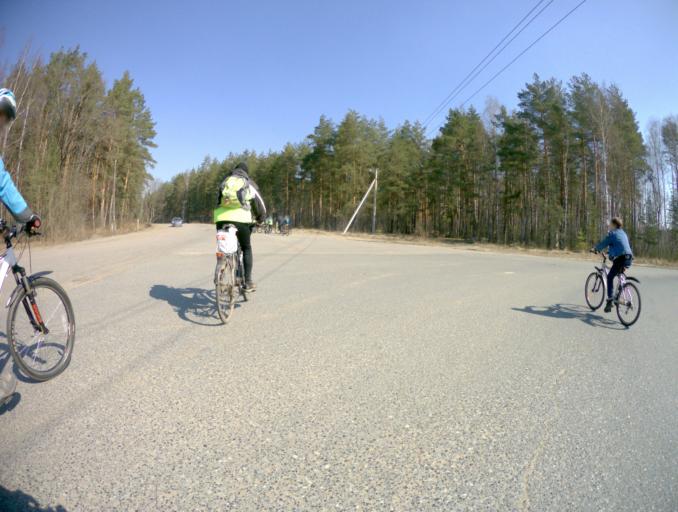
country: RU
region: Vladimir
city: Kommunar
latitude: 56.1319
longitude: 40.4893
